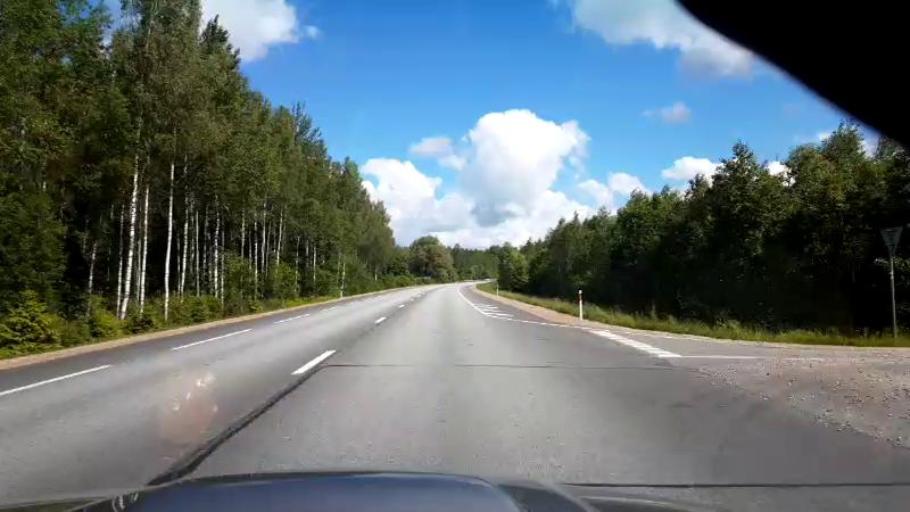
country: LV
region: Kekava
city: Kekava
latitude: 56.7160
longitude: 24.2489
